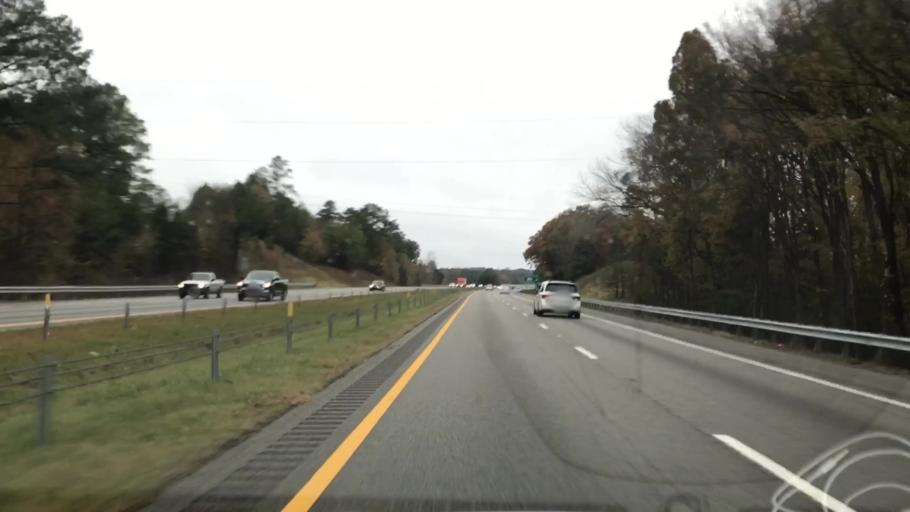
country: US
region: South Carolina
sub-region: Newberry County
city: Prosperity
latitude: 34.2883
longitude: -81.5382
